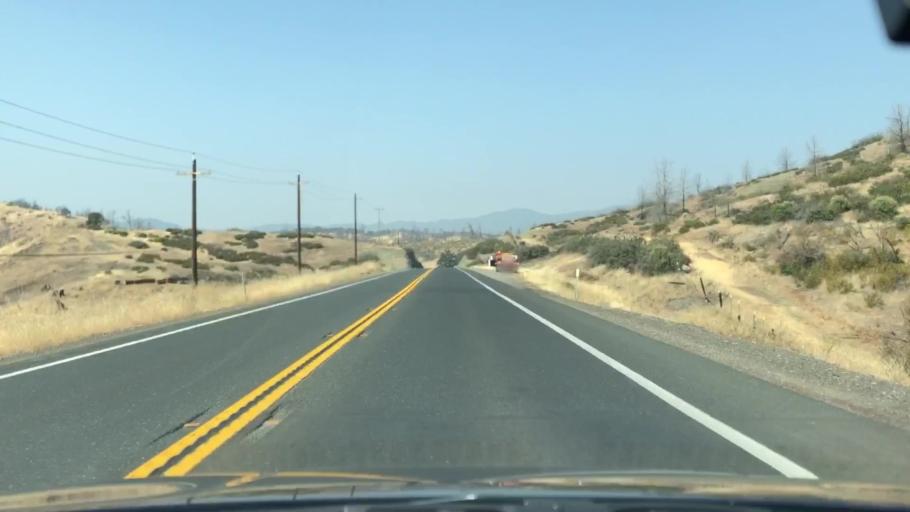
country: US
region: California
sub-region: Lake County
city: Hidden Valley Lake
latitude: 38.7770
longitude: -122.5773
